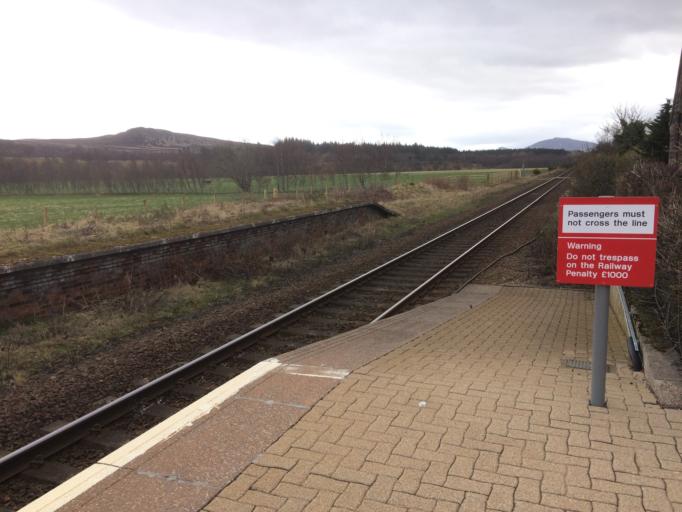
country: GB
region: Scotland
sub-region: Highland
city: Kingussie
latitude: 57.0591
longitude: -4.1190
